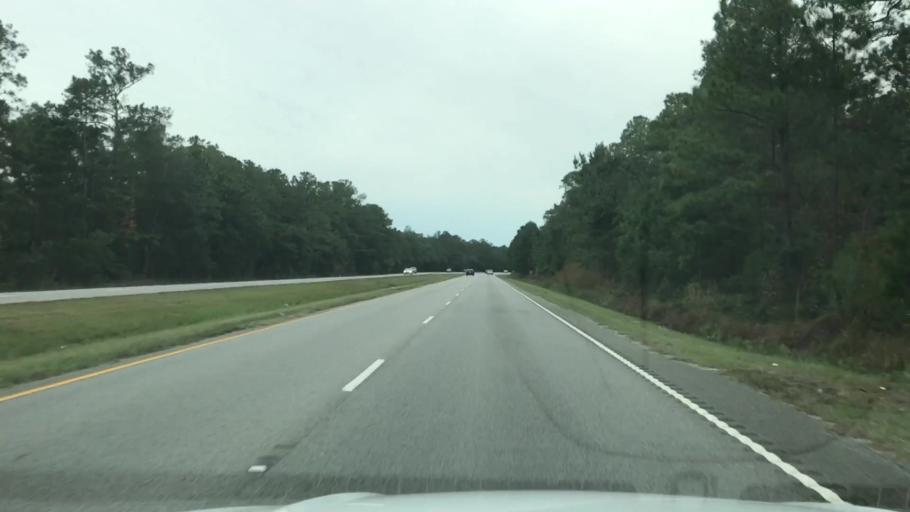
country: US
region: South Carolina
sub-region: Georgetown County
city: Georgetown
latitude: 33.3884
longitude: -79.2045
